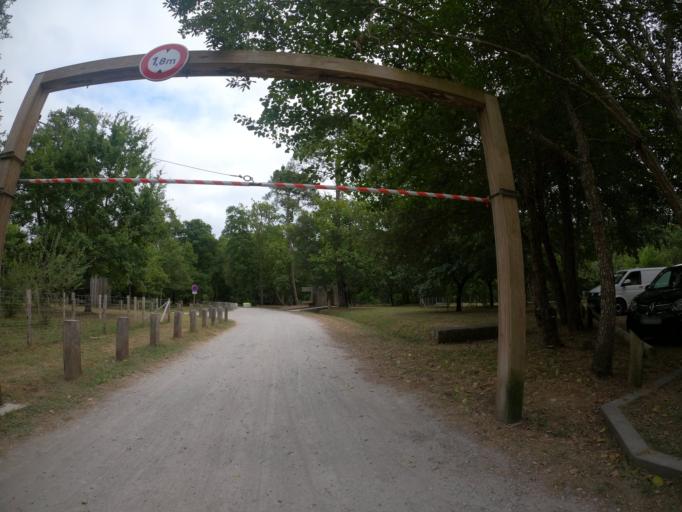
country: FR
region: Aquitaine
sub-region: Departement des Landes
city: Leon
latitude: 43.8873
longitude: -1.3151
